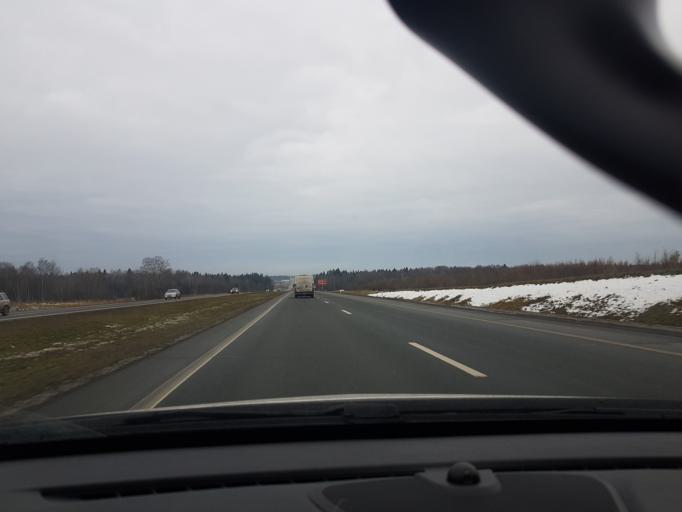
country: RU
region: Moskovskaya
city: Sychevo
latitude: 55.9908
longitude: 36.2623
